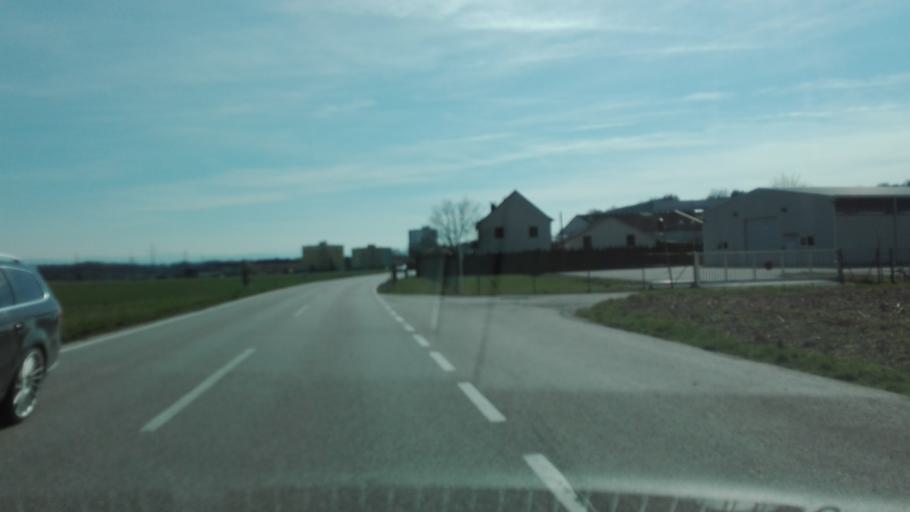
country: AT
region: Lower Austria
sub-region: Politischer Bezirk Amstetten
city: Ennsdorf
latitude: 48.2501
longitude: 14.5394
